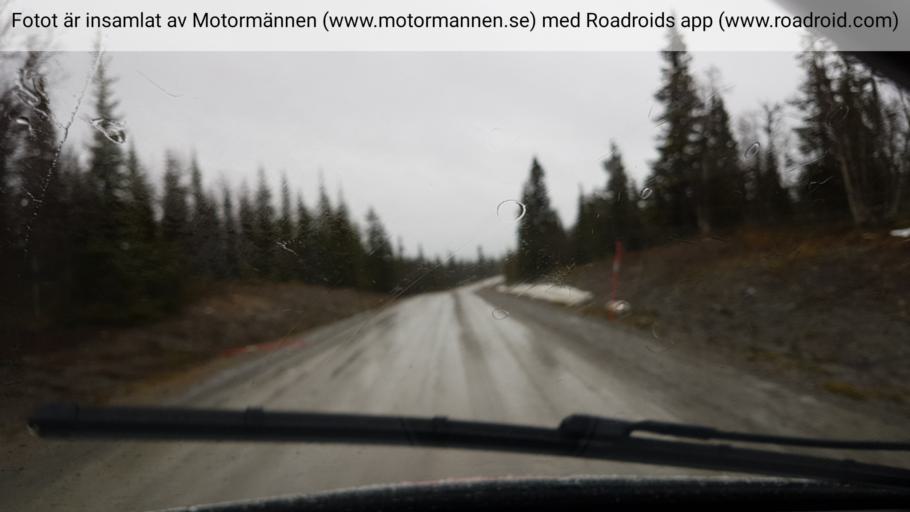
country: SE
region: Jaemtland
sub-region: Are Kommun
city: Are
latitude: 62.6578
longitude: 13.0309
